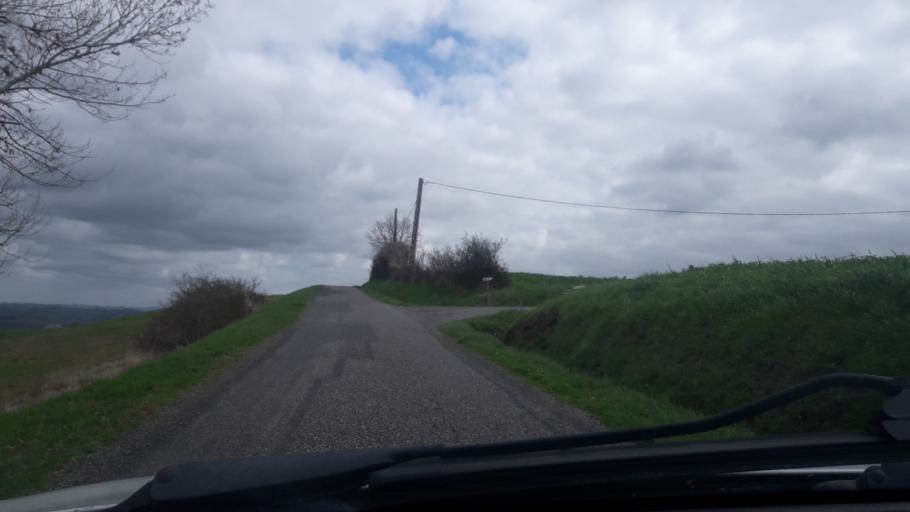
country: FR
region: Midi-Pyrenees
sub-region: Departement de l'Ariege
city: Lezat-sur-Leze
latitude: 43.1948
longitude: 1.3226
